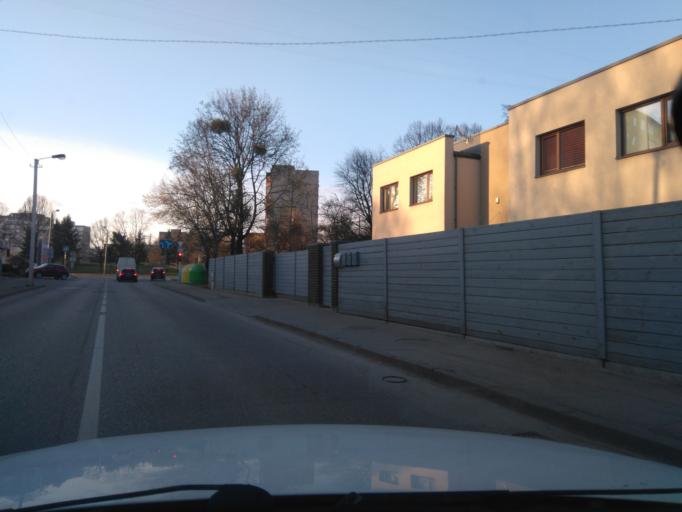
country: LT
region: Kauno apskritis
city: Dainava (Kaunas)
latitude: 54.9110
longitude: 23.9641
